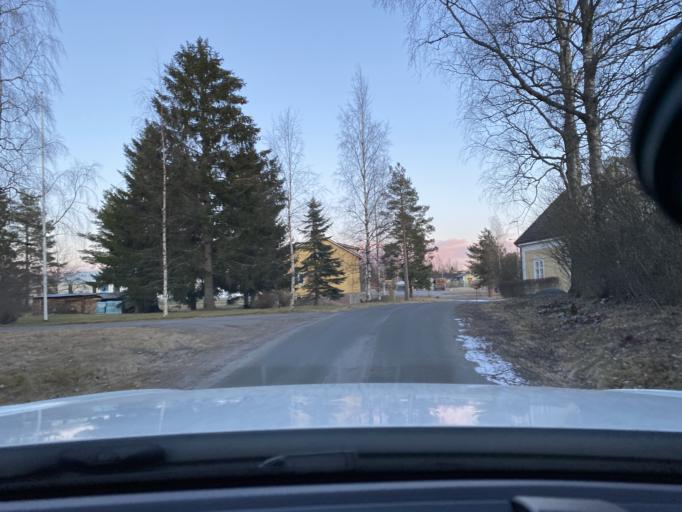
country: FI
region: Pirkanmaa
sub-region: Lounais-Pirkanmaa
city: Punkalaidun
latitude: 61.1185
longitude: 23.0836
